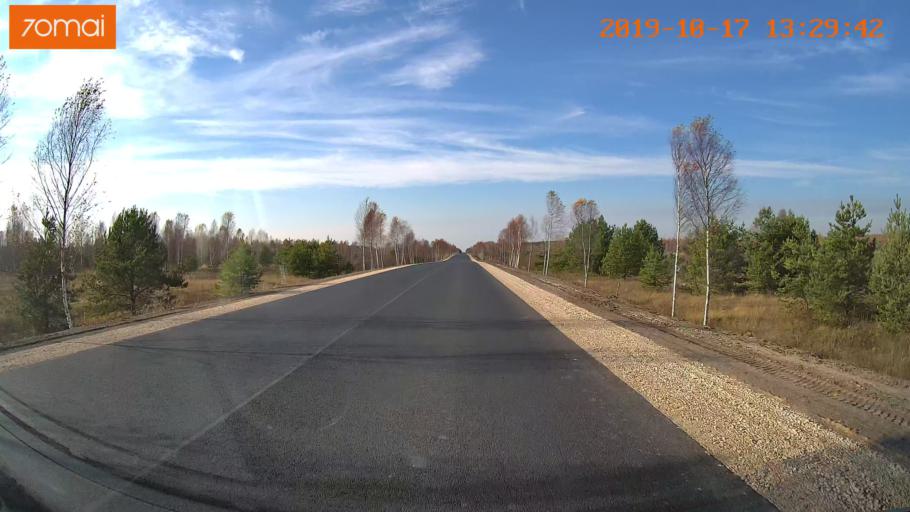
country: RU
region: Vladimir
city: Velikodvorskiy
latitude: 55.1207
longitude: 40.8348
